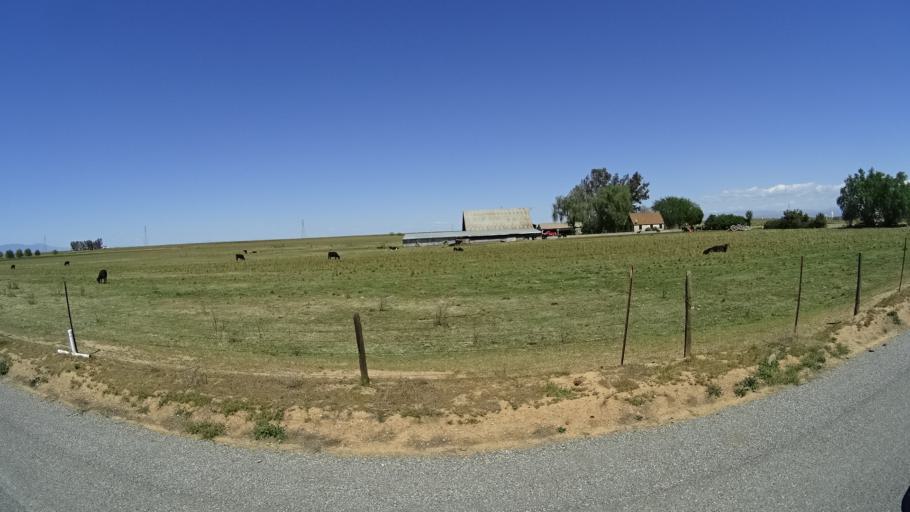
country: US
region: California
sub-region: Glenn County
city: Orland
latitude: 39.7935
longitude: -122.2219
